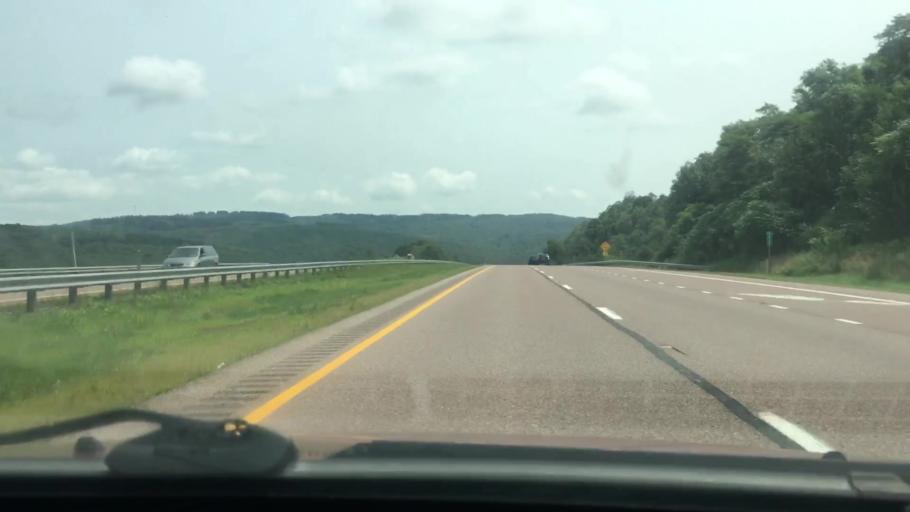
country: US
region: Pennsylvania
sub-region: Somerset County
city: Meyersdale
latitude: 39.7008
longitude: -79.2971
